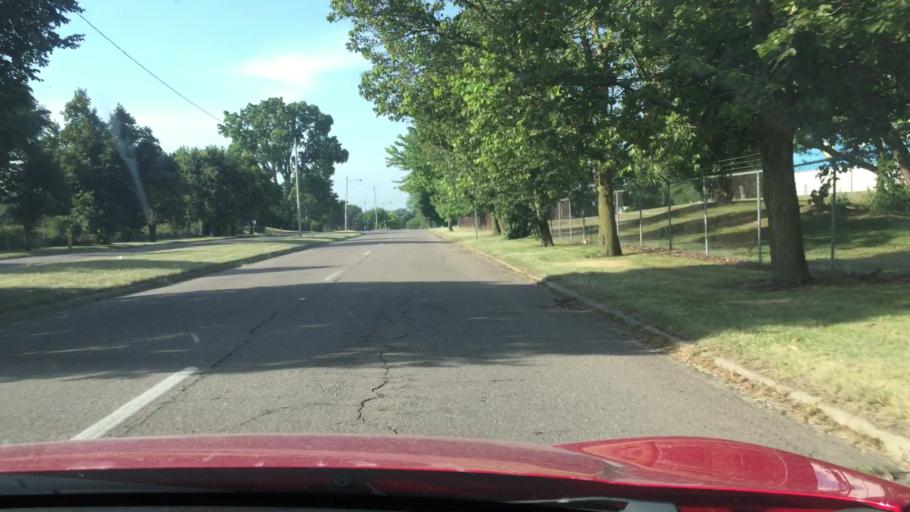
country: US
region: Michigan
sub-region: Genesee County
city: Flint
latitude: 43.0513
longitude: -83.6767
